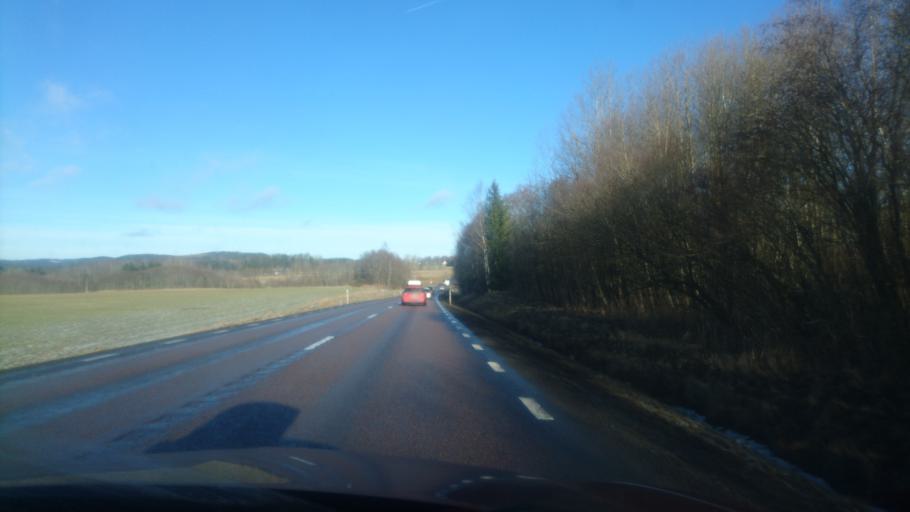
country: SE
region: Vaermland
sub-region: Sunne Kommun
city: Sunne
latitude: 59.7230
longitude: 13.1348
